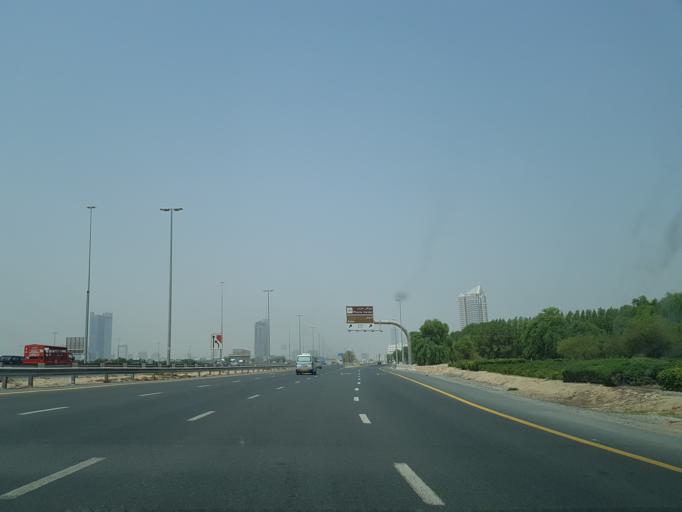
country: AE
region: Dubai
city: Dubai
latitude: 25.0560
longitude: 55.2460
